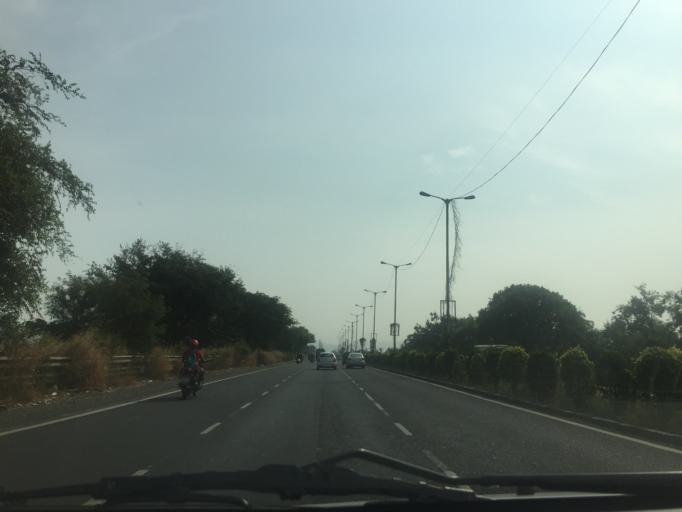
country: IN
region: Maharashtra
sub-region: Thane
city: Airoli
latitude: 19.1525
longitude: 72.9712
